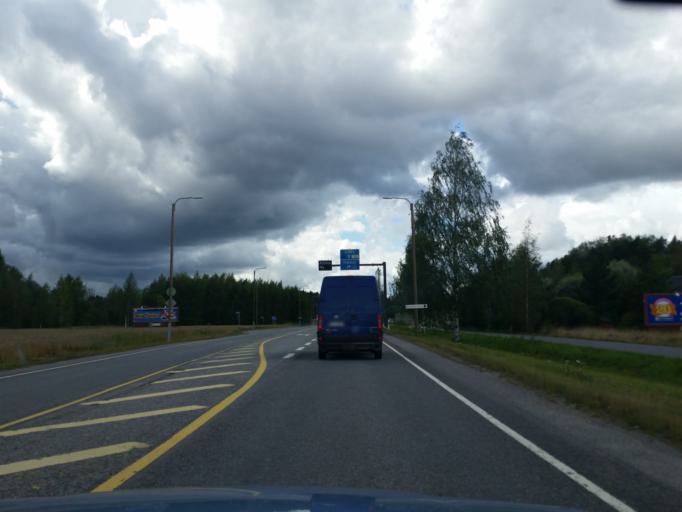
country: FI
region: Varsinais-Suomi
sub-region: Turku
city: Piikkioe
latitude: 60.4204
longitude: 22.4776
